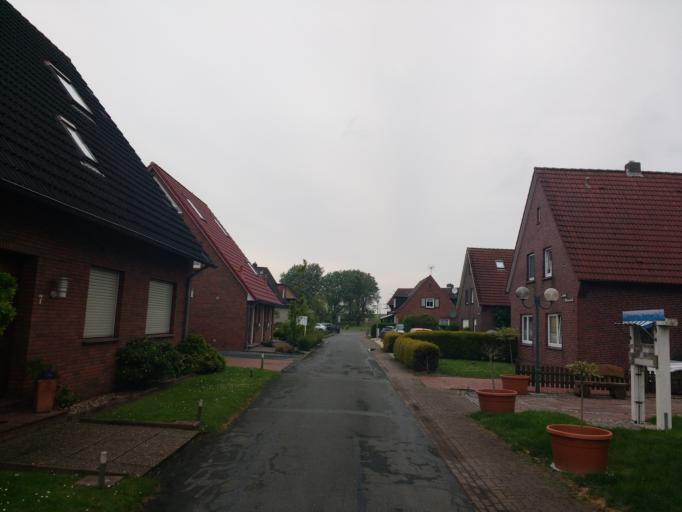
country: DE
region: Lower Saxony
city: Neuharlingersiel
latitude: 53.6988
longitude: 7.7077
